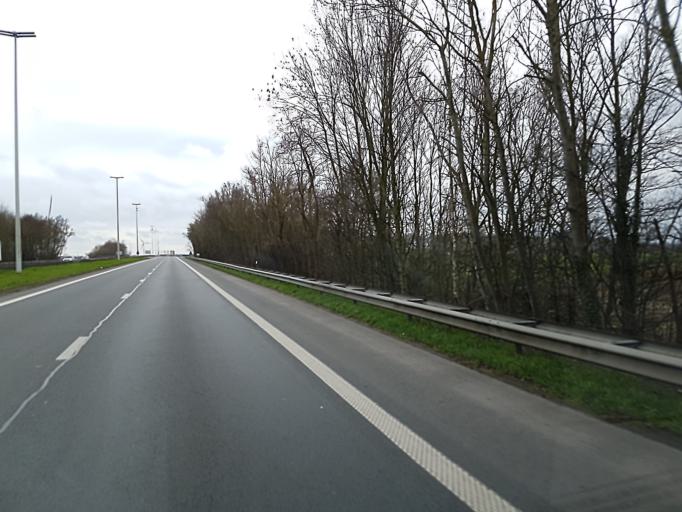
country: BE
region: Wallonia
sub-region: Province du Hainaut
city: Estaimpuis
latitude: 50.7034
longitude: 3.2970
